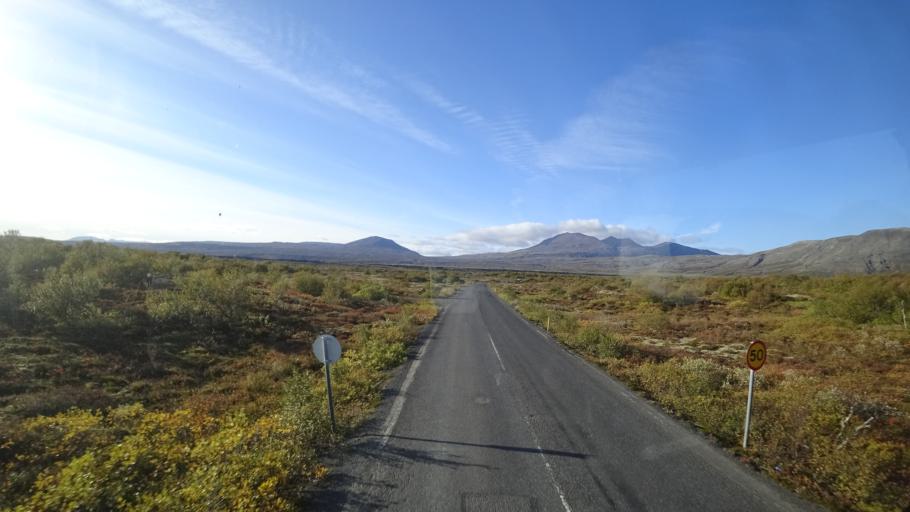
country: IS
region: South
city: Hveragerdi
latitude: 64.2722
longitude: -21.0698
